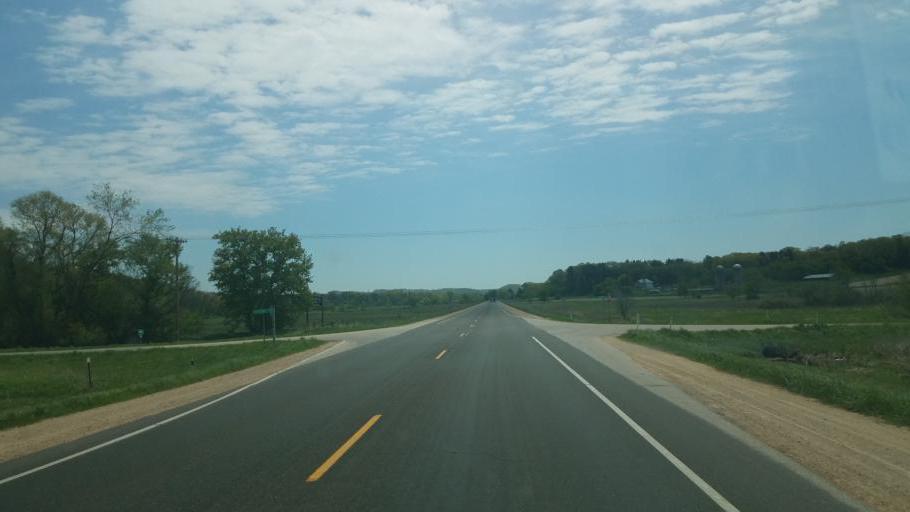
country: US
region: Wisconsin
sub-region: Monroe County
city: Tomah
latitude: 43.9474
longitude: -90.5040
